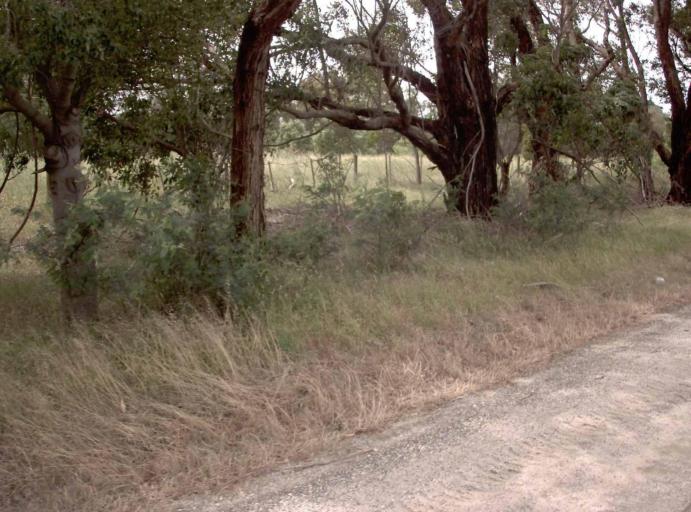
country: AU
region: Victoria
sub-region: Wellington
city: Sale
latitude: -37.9852
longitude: 146.9931
